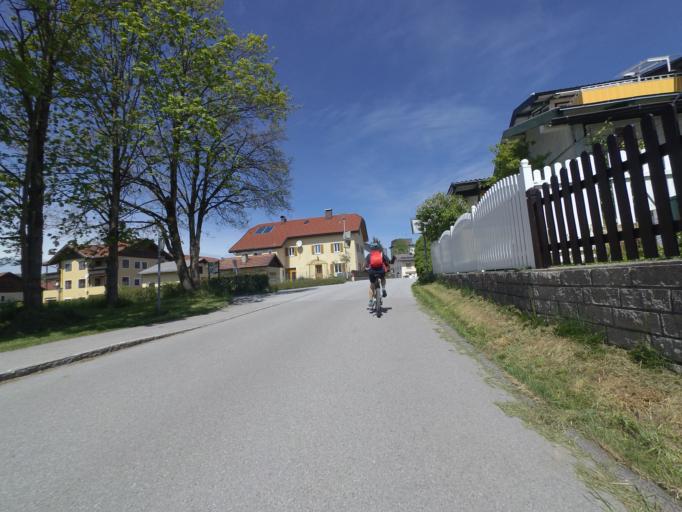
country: AT
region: Salzburg
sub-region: Politischer Bezirk Salzburg-Umgebung
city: Obertrum am See
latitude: 47.9353
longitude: 13.0793
